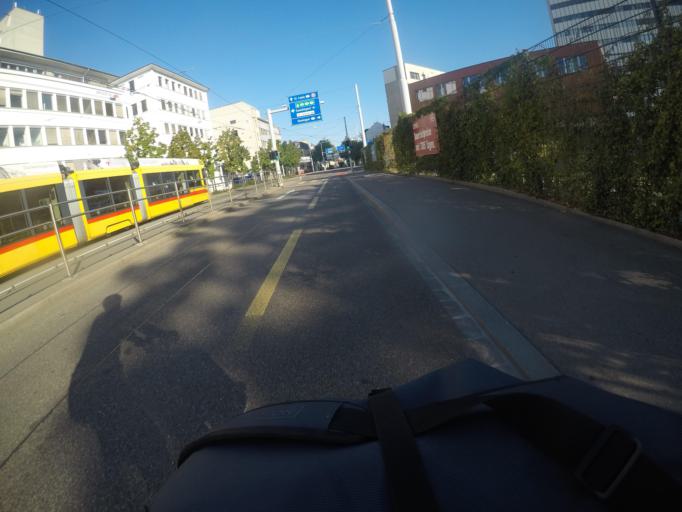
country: FR
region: Alsace
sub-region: Departement du Haut-Rhin
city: Village-Neuf
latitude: 47.5753
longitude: 7.5738
